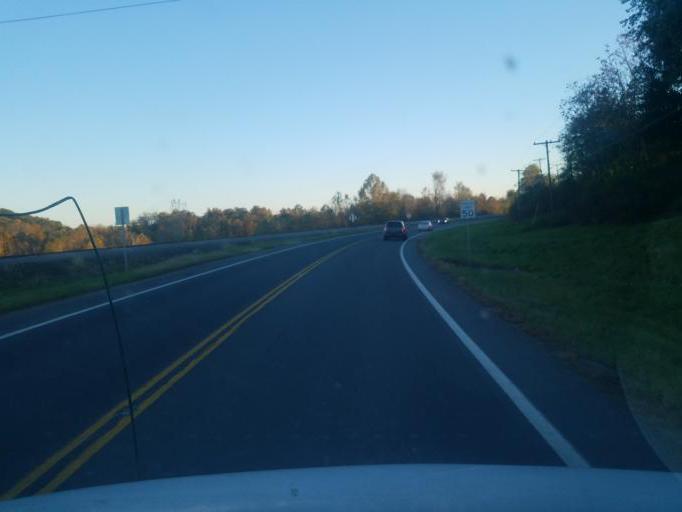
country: US
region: Ohio
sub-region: Licking County
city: Newark
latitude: 40.1202
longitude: -82.4287
